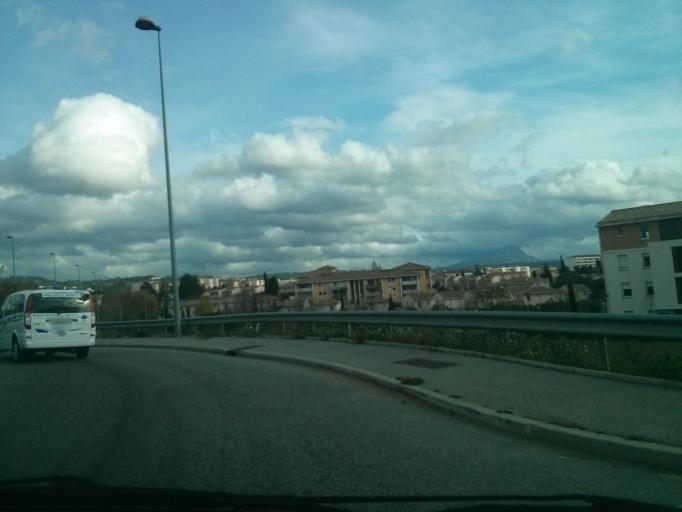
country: FR
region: Provence-Alpes-Cote d'Azur
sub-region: Departement des Bouches-du-Rhone
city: Aix-en-Provence
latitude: 43.5281
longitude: 5.4058
